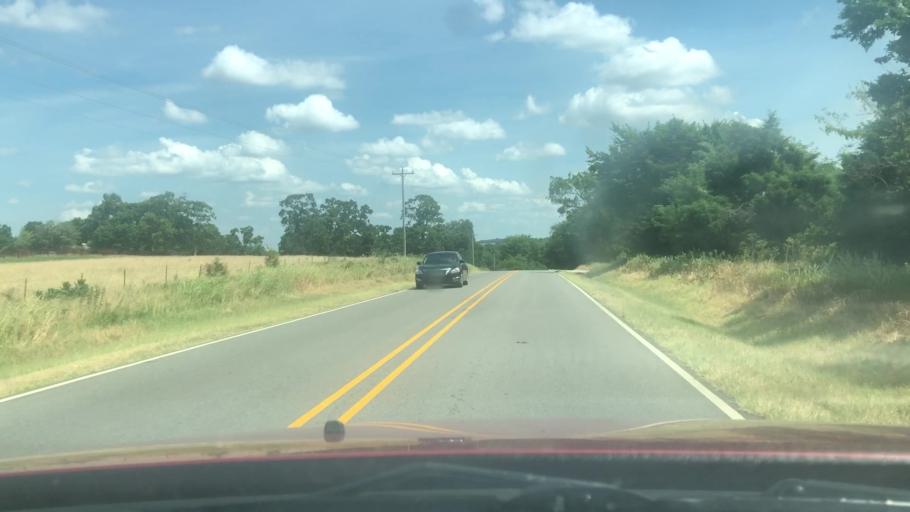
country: US
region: Arkansas
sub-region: Carroll County
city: Berryville
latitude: 36.3987
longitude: -93.5477
